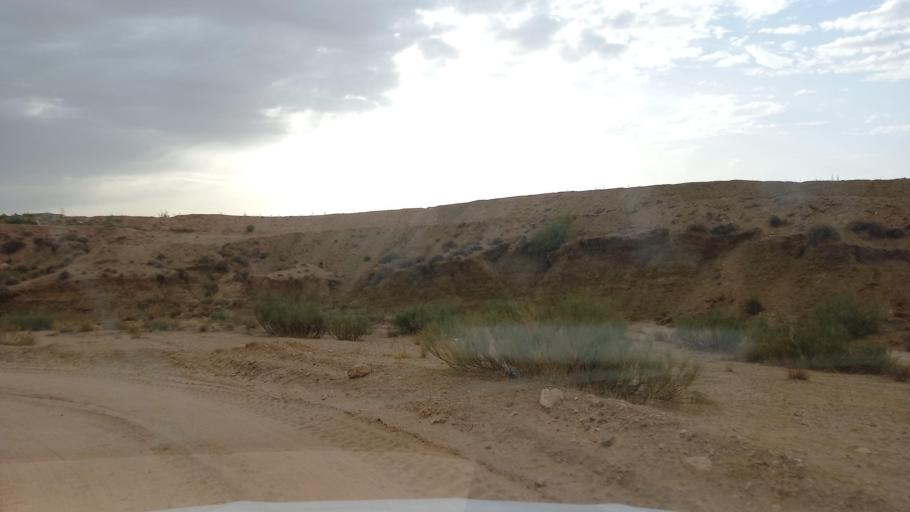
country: TN
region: Al Qasrayn
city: Kasserine
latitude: 35.1865
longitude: 9.0576
